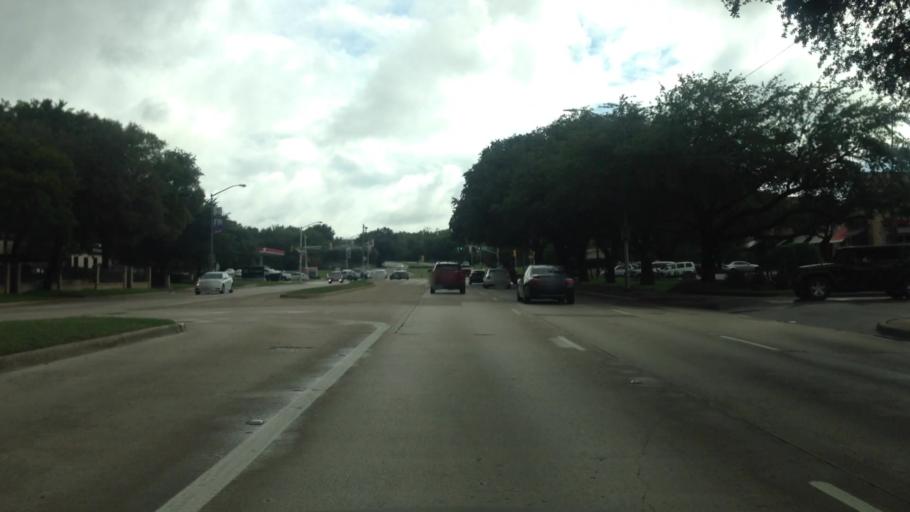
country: US
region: Texas
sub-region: Tarrant County
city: Westworth
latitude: 32.7057
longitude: -97.3884
